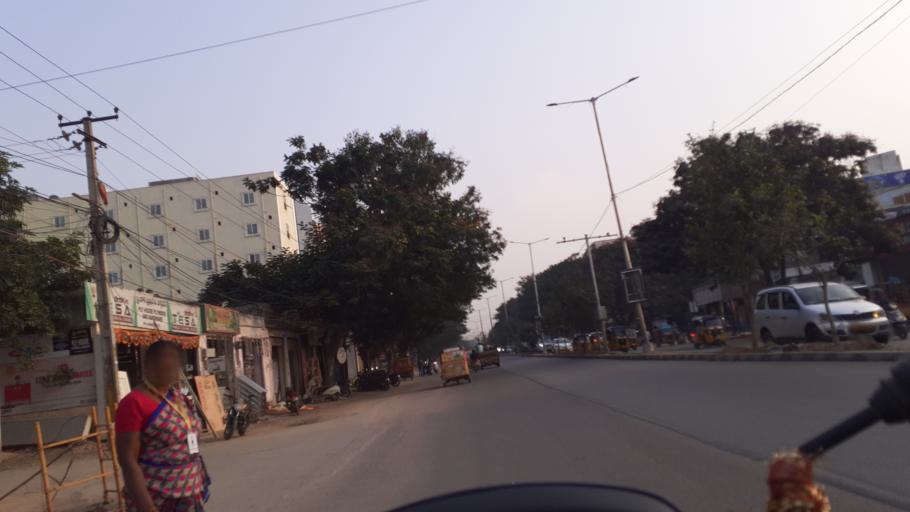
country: IN
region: Telangana
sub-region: Rangareddi
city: Kukatpalli
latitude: 17.4749
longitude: 78.3636
